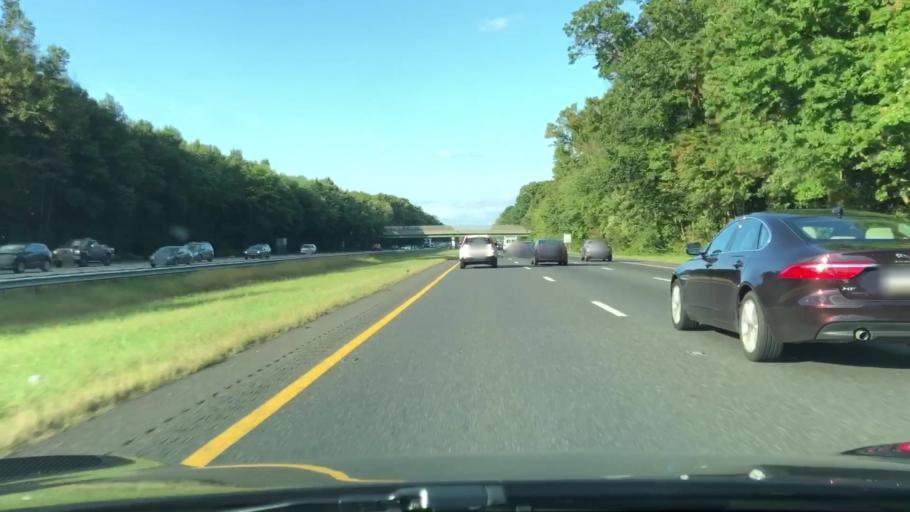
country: US
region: New Jersey
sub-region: Burlington County
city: Willingboro
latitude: 40.0194
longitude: -74.8456
